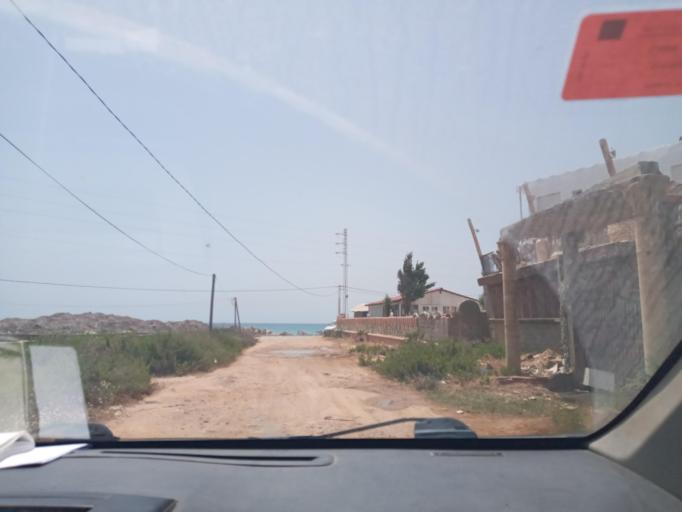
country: TN
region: Nabul
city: El Haouaria
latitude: 37.0417
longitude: 11.0619
